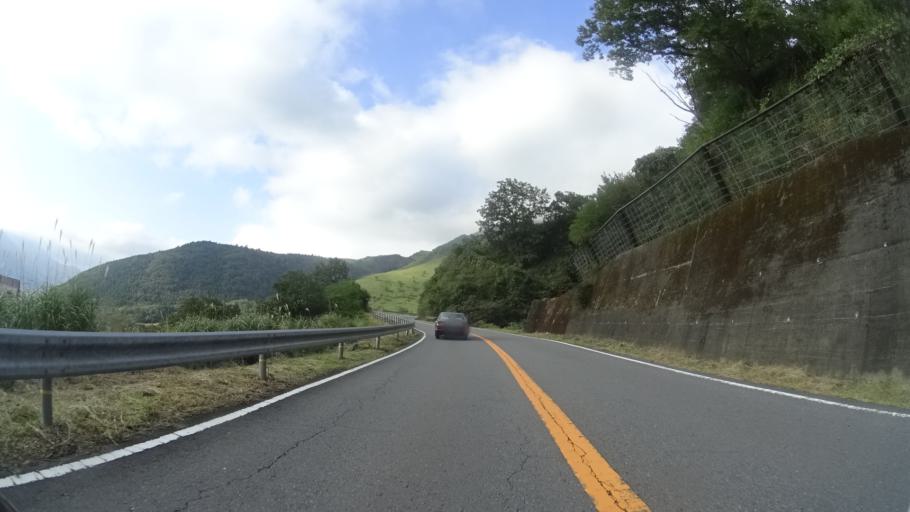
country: JP
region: Oita
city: Beppu
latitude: 33.2590
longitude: 131.3813
